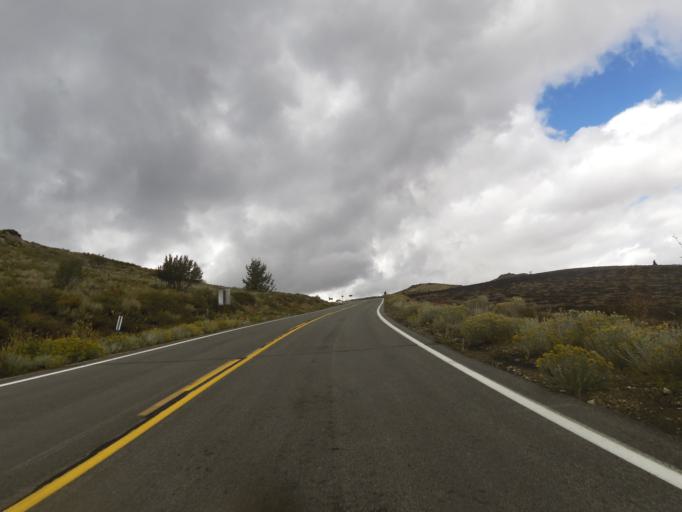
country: US
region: Nevada
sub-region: Douglas County
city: Gardnerville Ranchos
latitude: 38.6783
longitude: -119.5920
